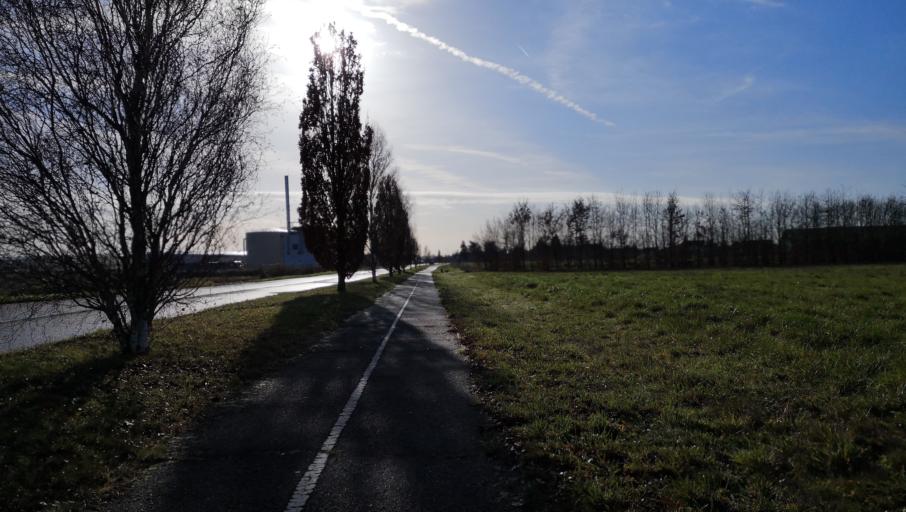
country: FR
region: Centre
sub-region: Departement du Loiret
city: Saint-Denis-en-Val
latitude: 47.8762
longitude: 1.9793
